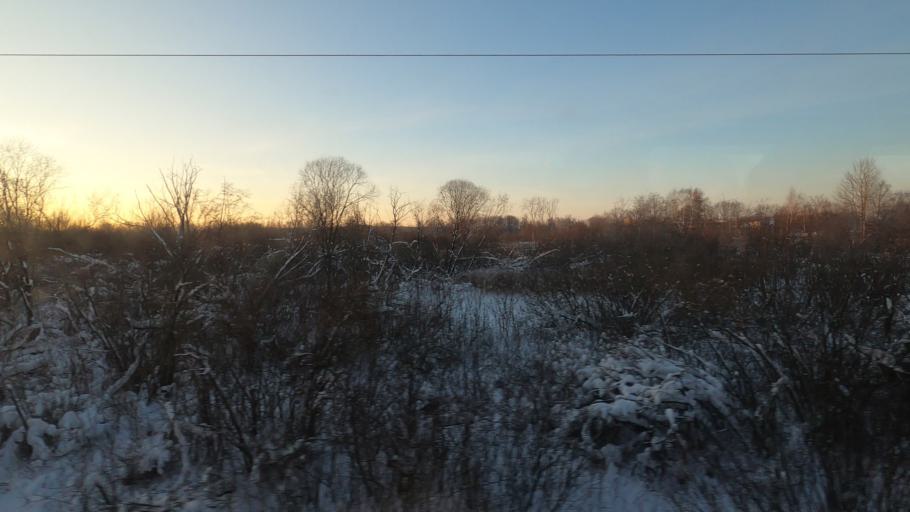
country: RU
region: Moskovskaya
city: Dmitrov
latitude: 56.3607
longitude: 37.5225
